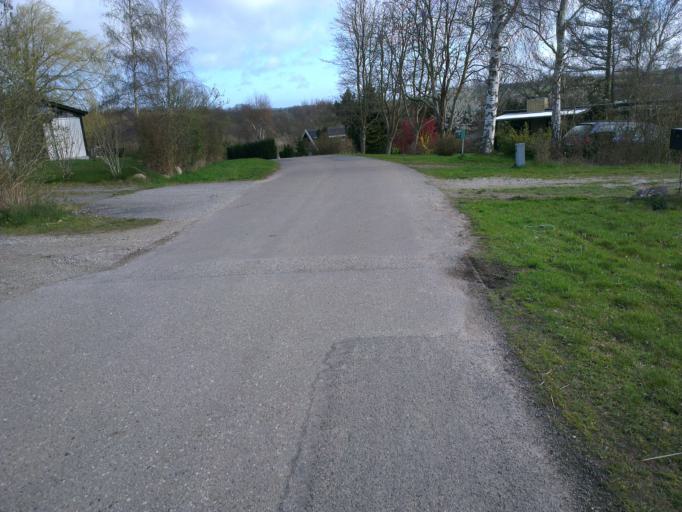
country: DK
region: Capital Region
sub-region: Frederikssund Kommune
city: Jaegerspris
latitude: 55.8338
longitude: 11.9731
